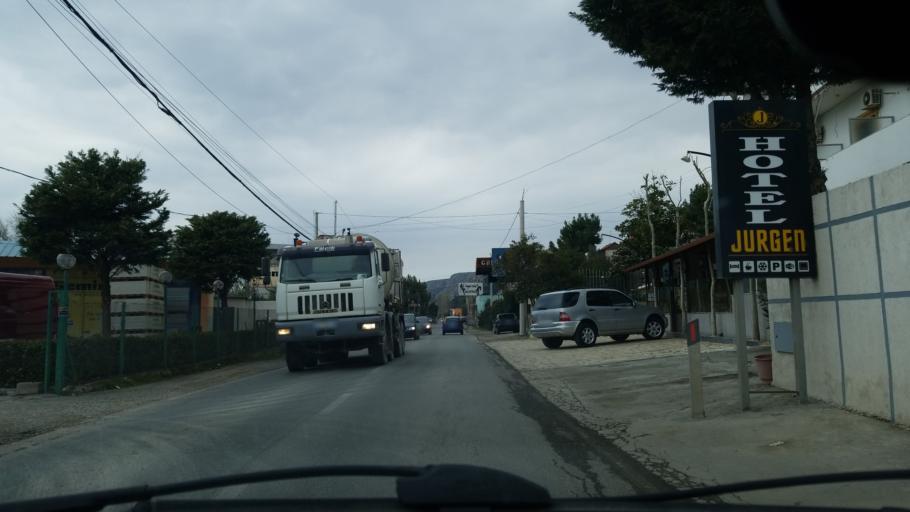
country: AL
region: Lezhe
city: Lezhe
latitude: 41.7784
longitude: 19.6333
